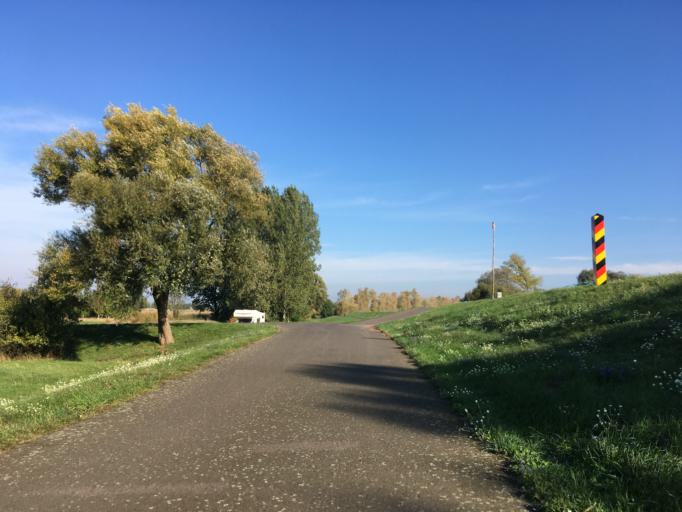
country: DE
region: Brandenburg
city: Reitwein
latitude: 52.5453
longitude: 14.6091
